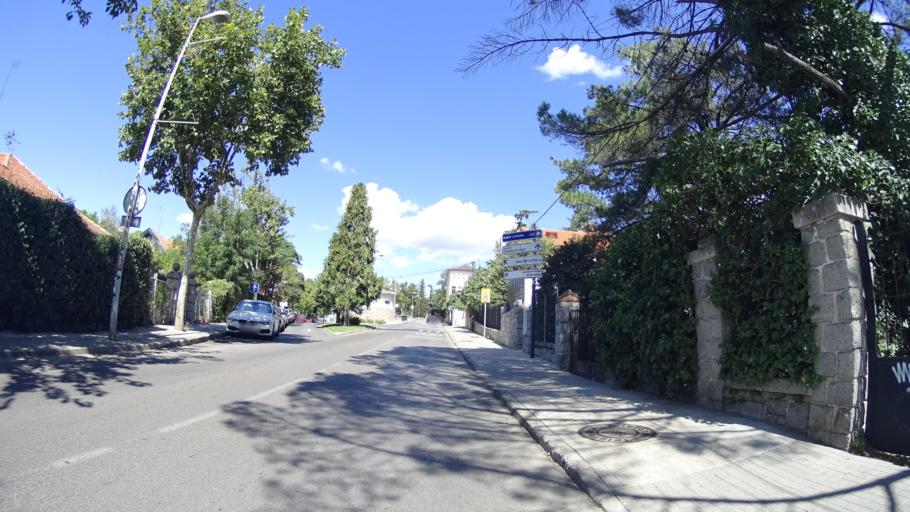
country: ES
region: Madrid
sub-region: Provincia de Madrid
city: Torrelodones
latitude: 40.5738
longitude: -3.9538
